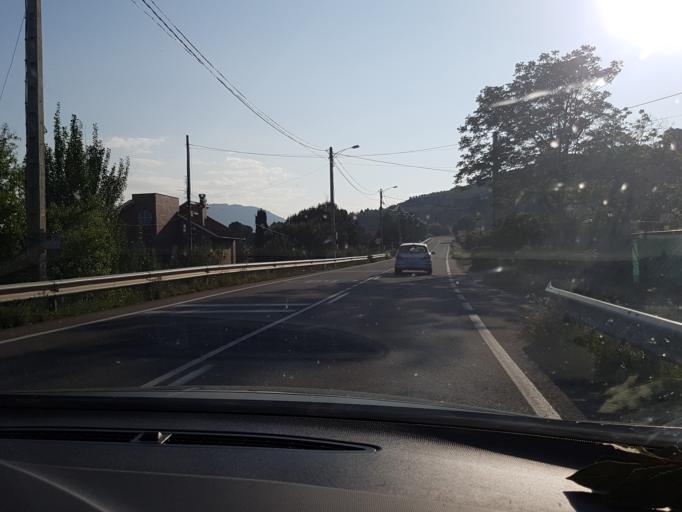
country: ES
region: La Rioja
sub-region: Provincia de La Rioja
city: Arnedo
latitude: 42.2203
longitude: -2.1130
